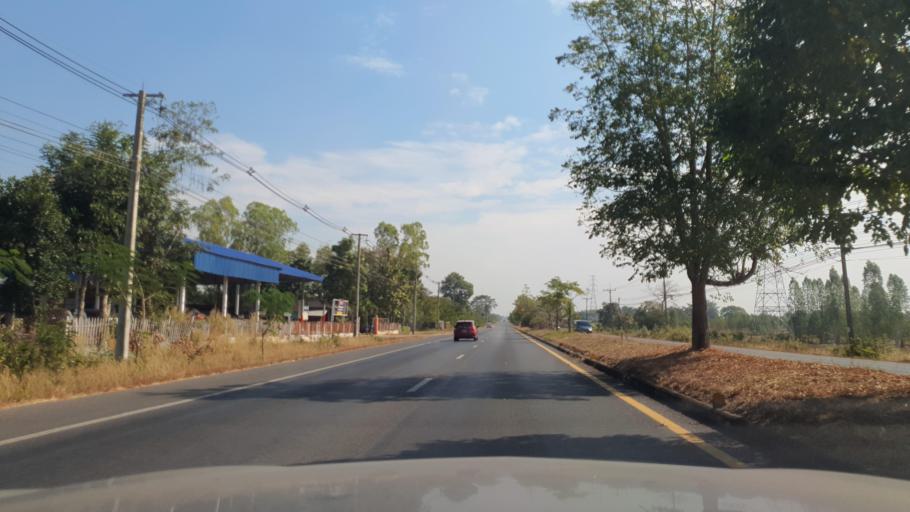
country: TH
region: Maha Sarakham
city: Kantharawichai
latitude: 16.3909
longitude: 103.2761
